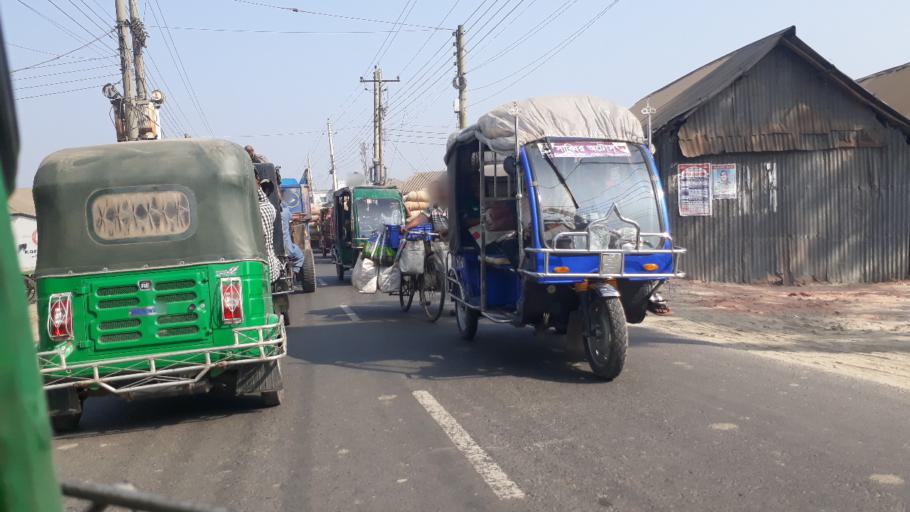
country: BD
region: Khulna
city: Kushtia
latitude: 23.8691
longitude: 89.0664
